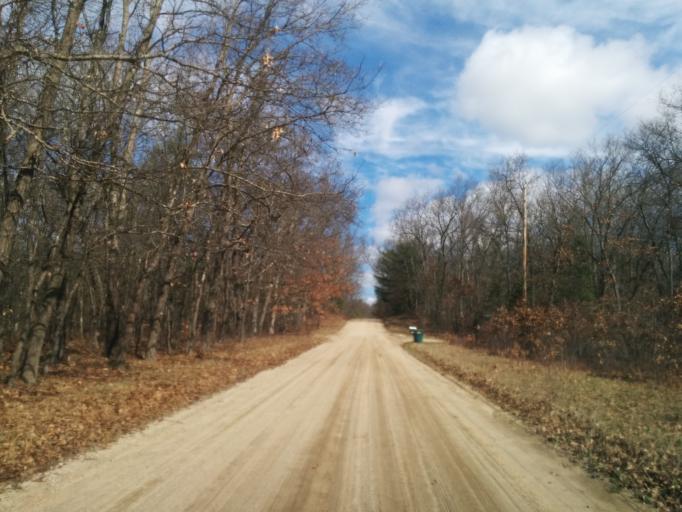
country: US
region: Michigan
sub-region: Newaygo County
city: Newaygo
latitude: 43.4307
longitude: -85.7276
